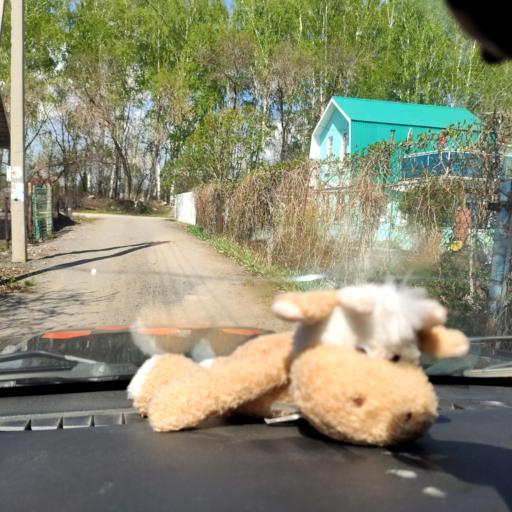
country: RU
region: Samara
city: Podstepki
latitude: 53.6070
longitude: 49.2210
